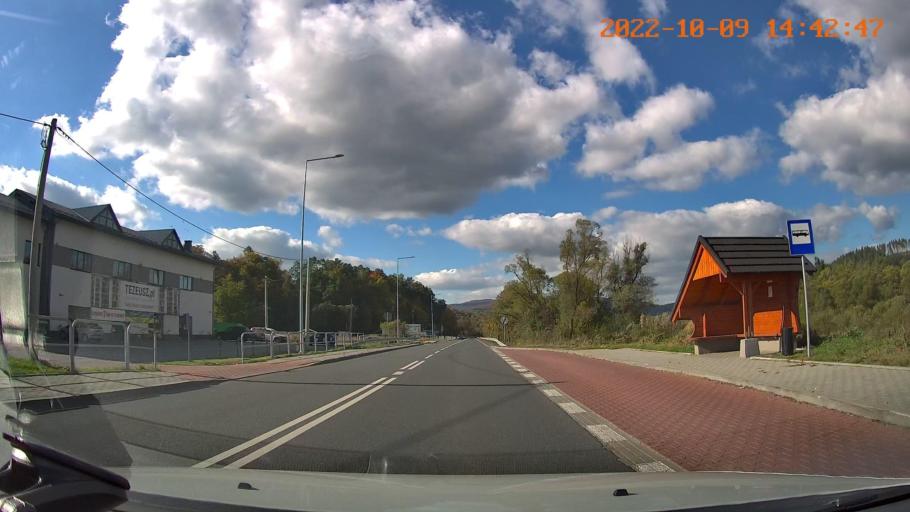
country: PL
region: Lesser Poland Voivodeship
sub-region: Powiat myslenicki
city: Lubien
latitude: 49.7160
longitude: 19.9924
